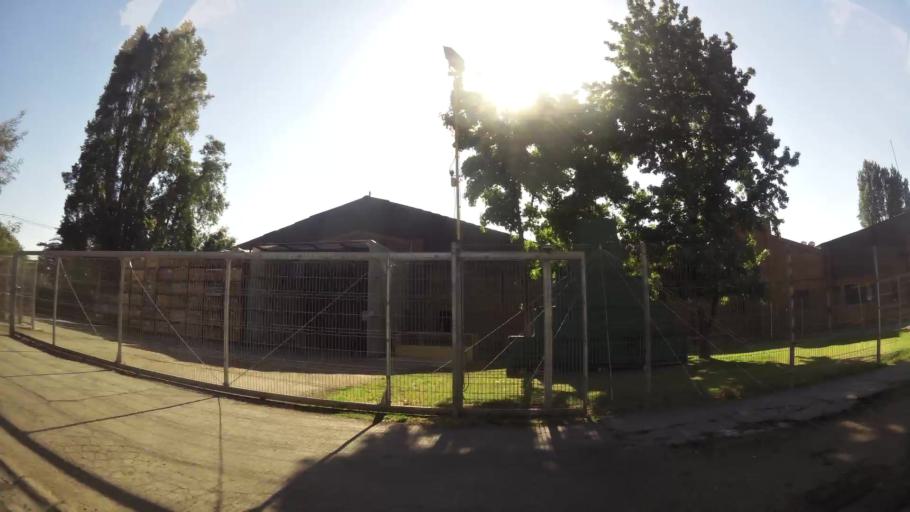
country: CL
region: Santiago Metropolitan
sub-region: Provincia de Maipo
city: San Bernardo
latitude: -33.6396
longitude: -70.6808
